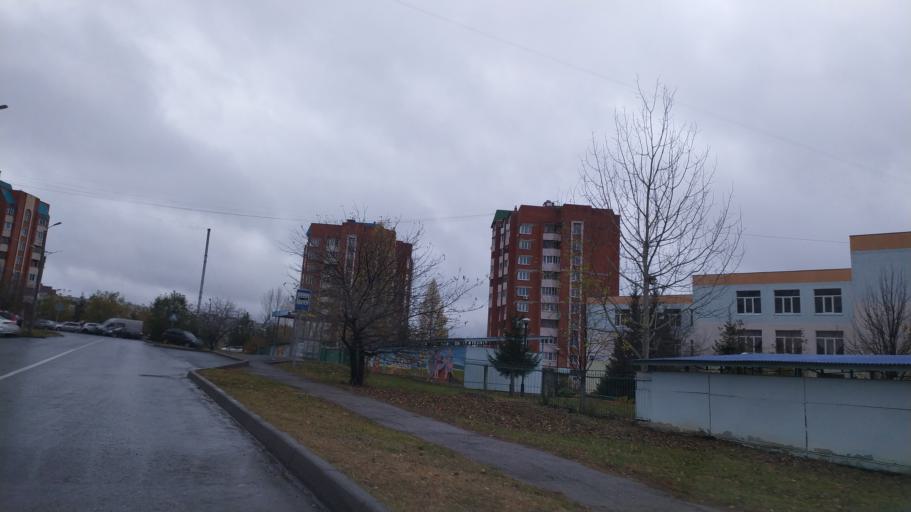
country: RU
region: Chuvashia
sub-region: Cheboksarskiy Rayon
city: Cheboksary
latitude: 56.1445
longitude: 47.1614
